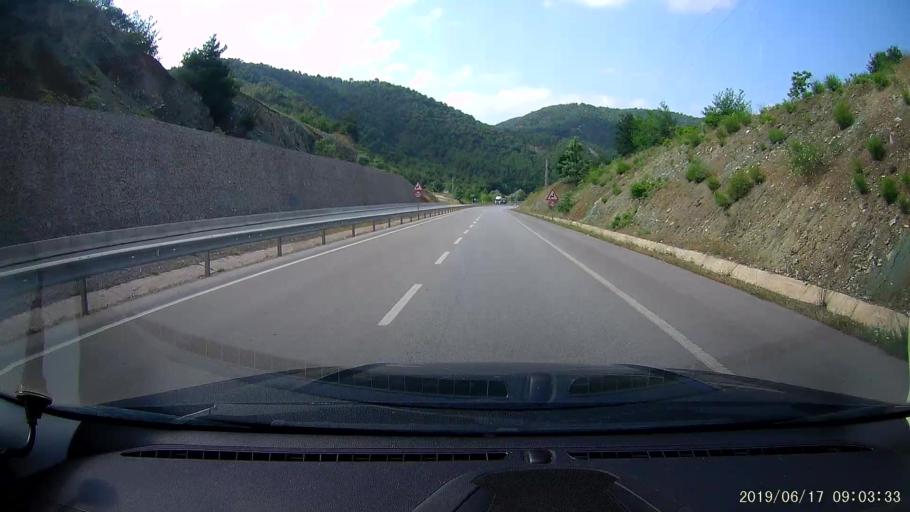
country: TR
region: Amasya
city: Tasova
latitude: 40.7541
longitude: 36.3023
